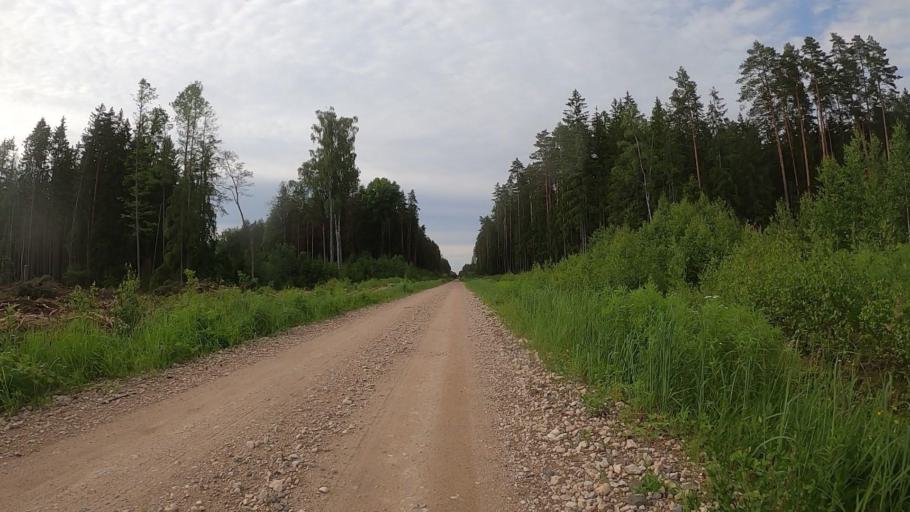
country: LV
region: Ozolnieku
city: Ozolnieki
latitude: 56.7325
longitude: 23.7909
